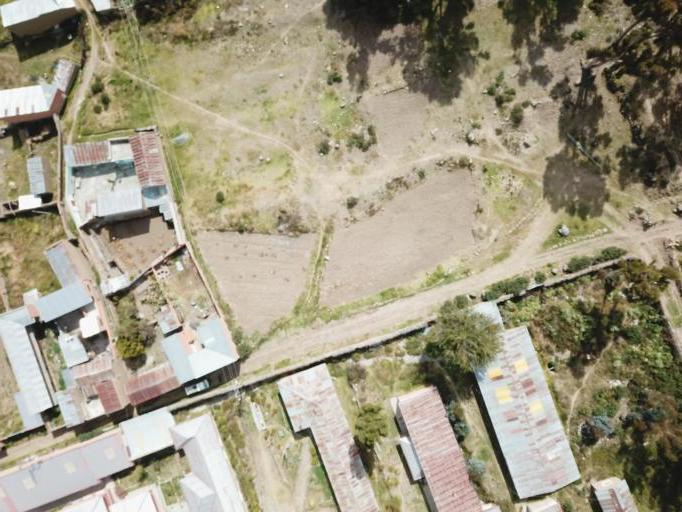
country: BO
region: La Paz
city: Achacachi
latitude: -16.0527
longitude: -68.8128
